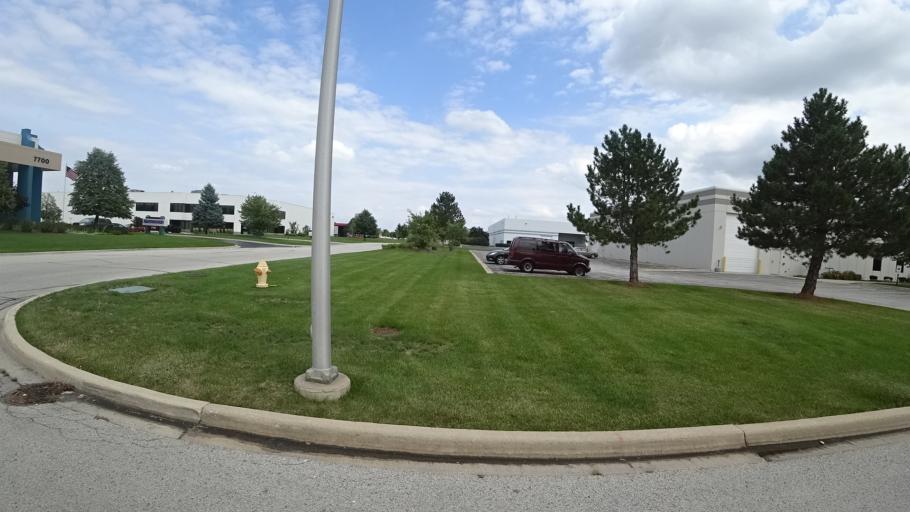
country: US
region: Illinois
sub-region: Cook County
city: Tinley Park
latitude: 41.5546
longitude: -87.8057
